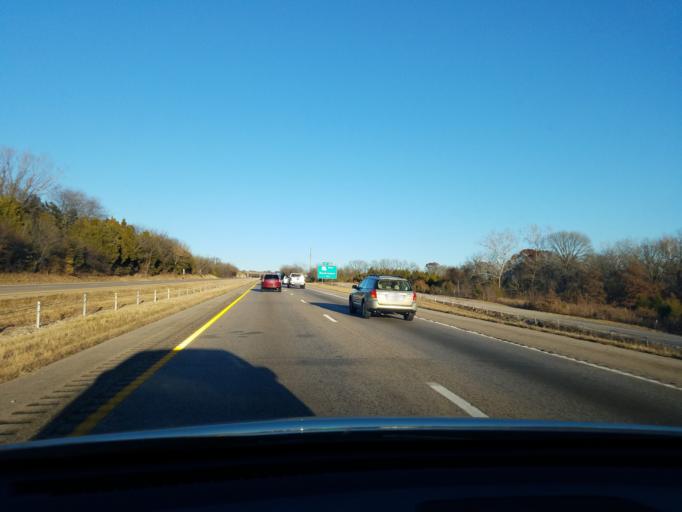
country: US
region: Missouri
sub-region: Franklin County
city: Villa Ridge
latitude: 38.4599
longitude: -90.8670
